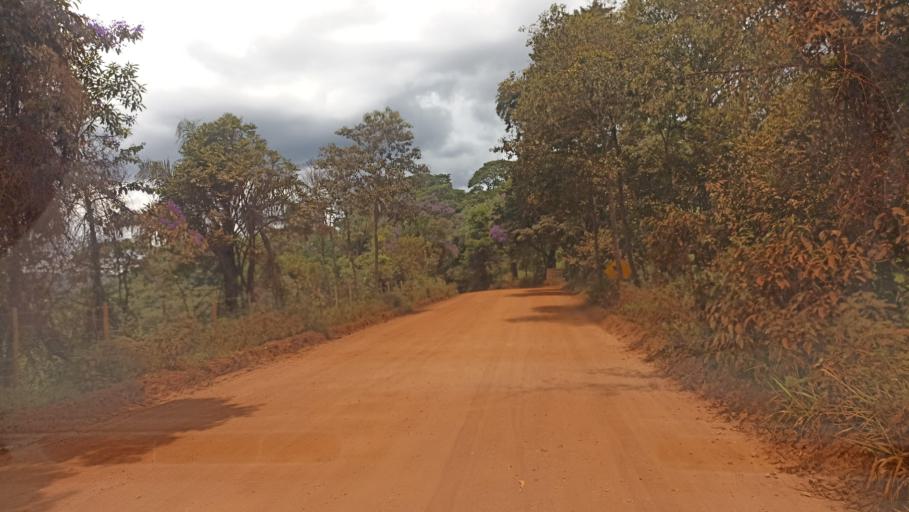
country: BR
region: Minas Gerais
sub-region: Itabirito
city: Itabirito
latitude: -20.3443
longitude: -43.7717
